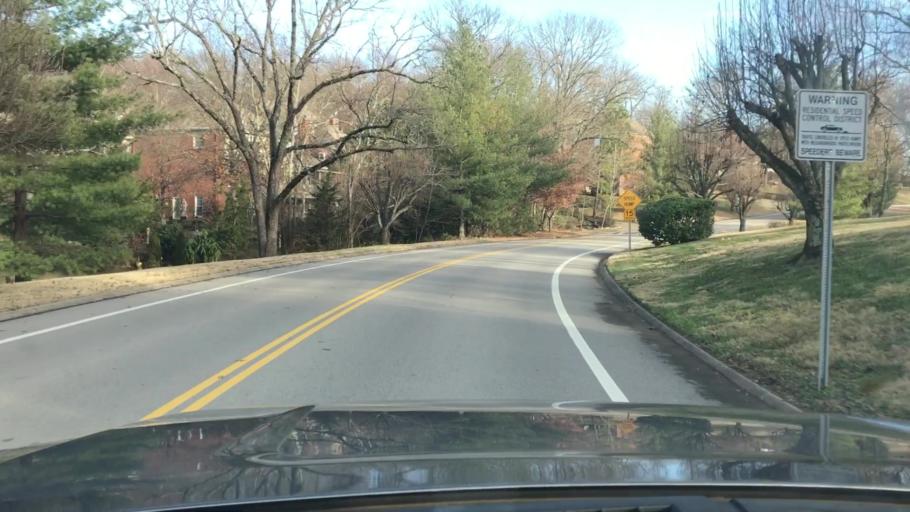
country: US
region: Tennessee
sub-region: Williamson County
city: Brentwood Estates
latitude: 35.9774
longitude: -86.7494
